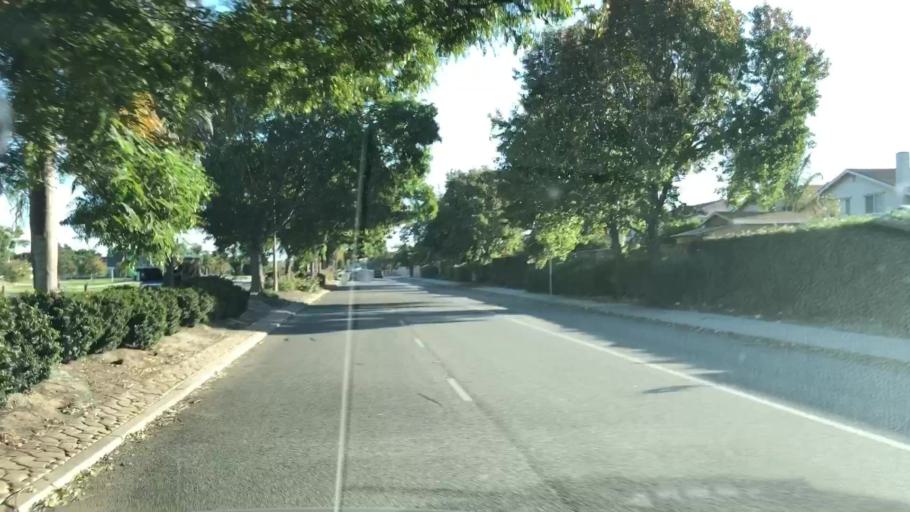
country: US
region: California
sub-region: Ventura County
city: Oxnard
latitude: 34.1663
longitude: -119.1595
